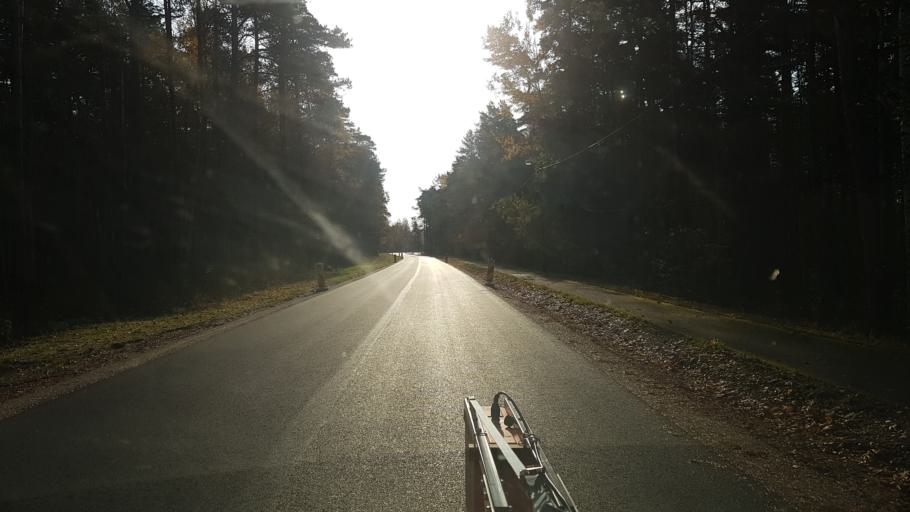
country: EE
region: Paernumaa
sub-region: Paikuse vald
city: Paikuse
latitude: 58.3660
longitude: 24.6020
